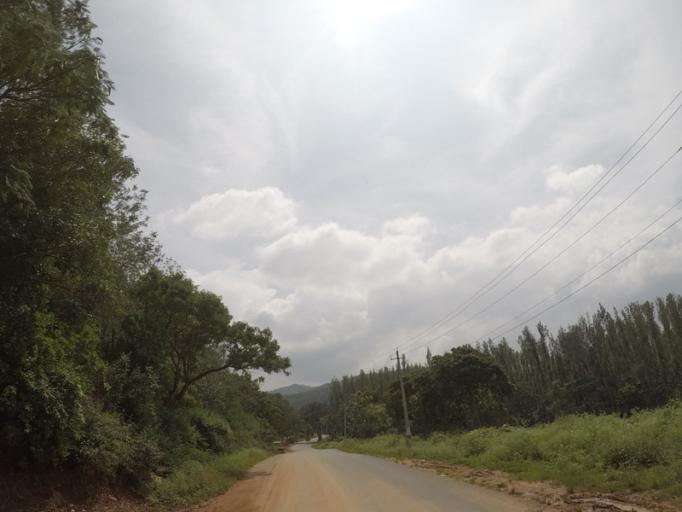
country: IN
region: Karnataka
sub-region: Chikmagalur
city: Chikmagalur
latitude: 13.3956
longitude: 75.7803
